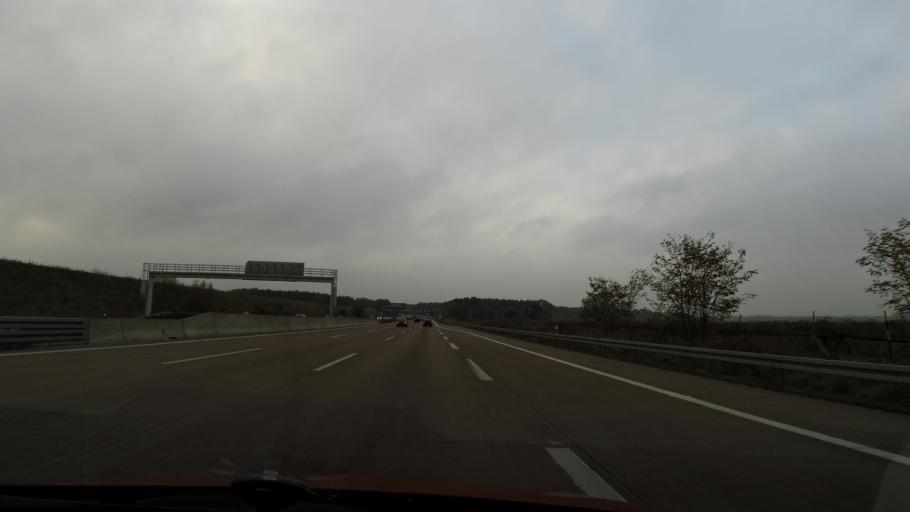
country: DE
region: Brandenburg
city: Michendorf
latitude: 52.3010
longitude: 13.0563
